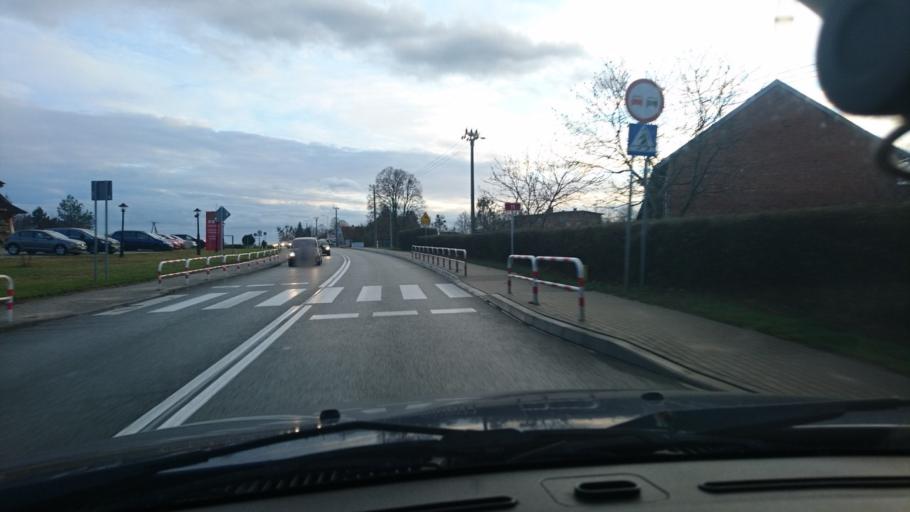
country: PL
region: Opole Voivodeship
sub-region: Powiat kluczborski
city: Kluczbork
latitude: 51.0277
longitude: 18.1918
